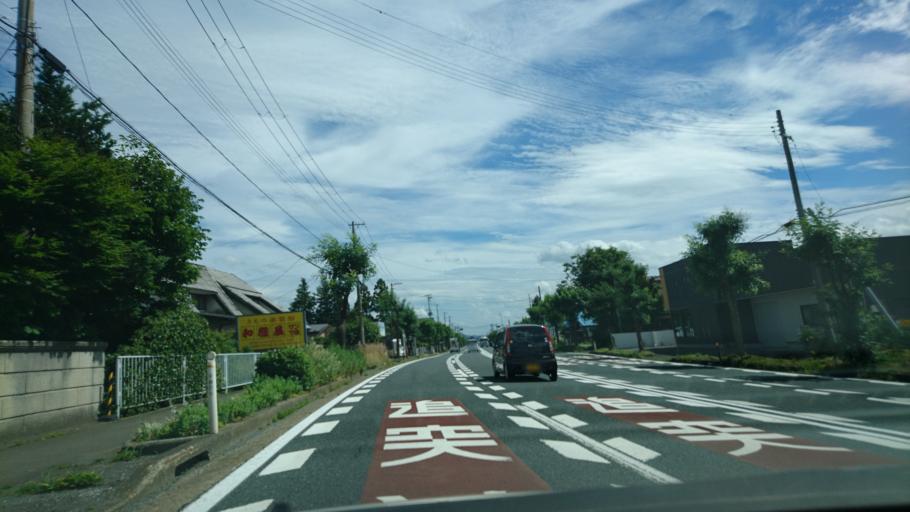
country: JP
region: Iwate
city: Morioka-shi
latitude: 39.6355
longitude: 141.1727
